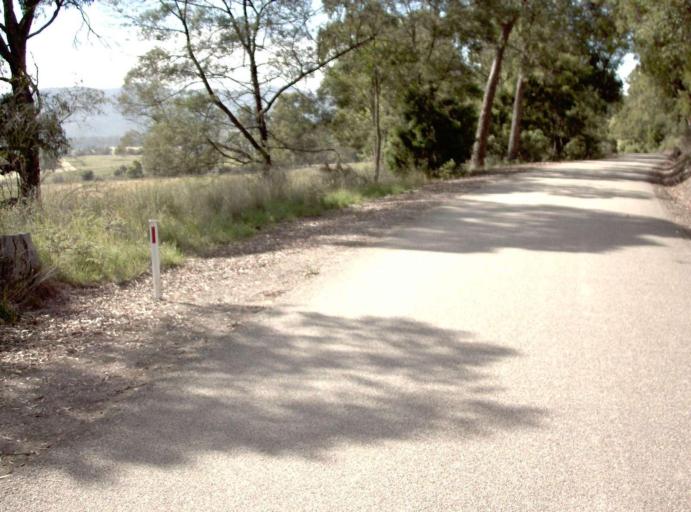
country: AU
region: Victoria
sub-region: East Gippsland
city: Lakes Entrance
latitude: -37.5220
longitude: 148.1399
